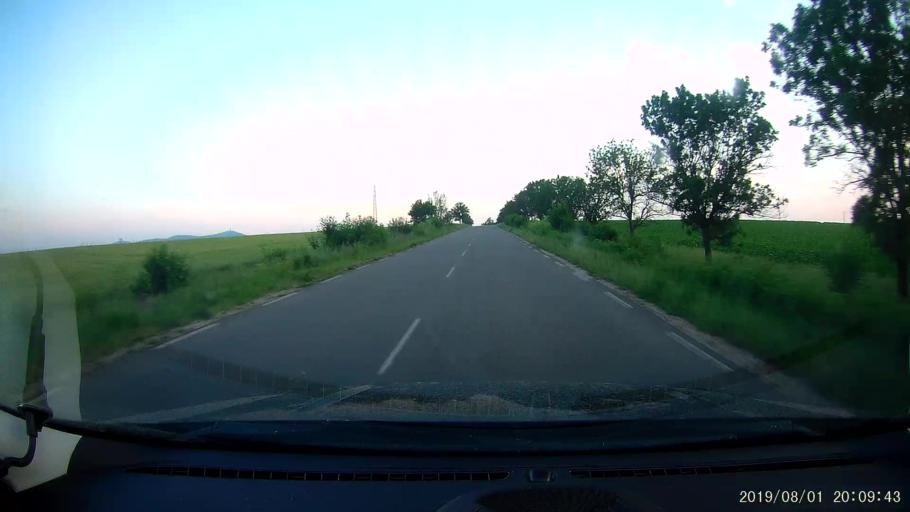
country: BG
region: Yambol
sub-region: Obshtina Yambol
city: Yambol
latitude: 42.4941
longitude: 26.5938
